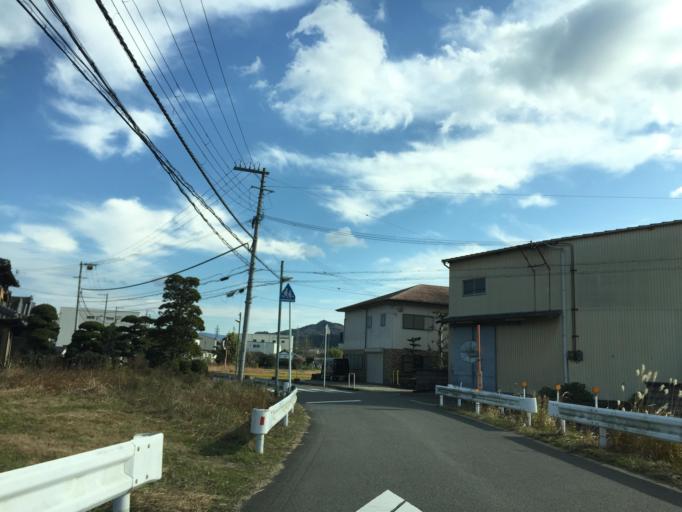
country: JP
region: Wakayama
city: Kainan
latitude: 34.1589
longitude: 135.2689
